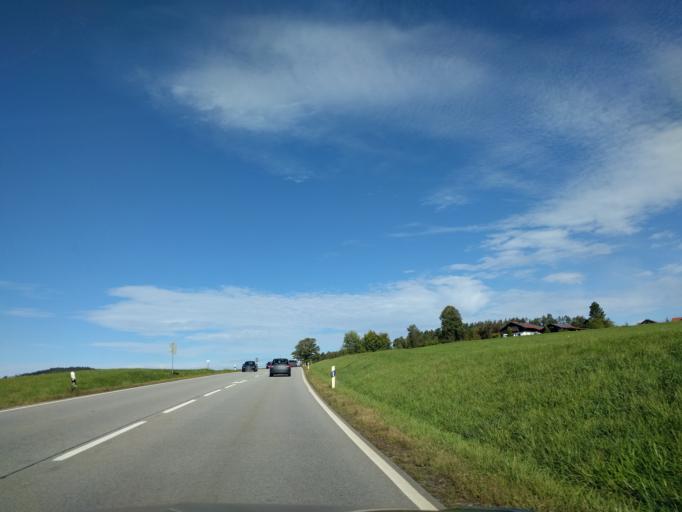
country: DE
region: Bavaria
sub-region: Lower Bavaria
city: Patersdorf
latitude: 49.0164
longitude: 12.9790
